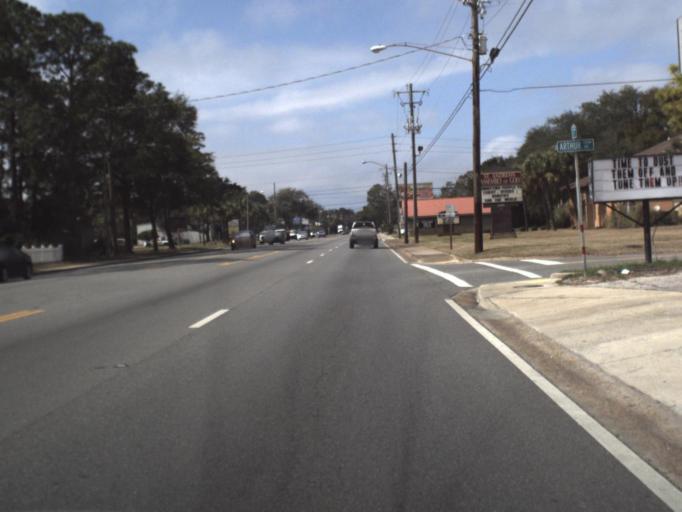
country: US
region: Florida
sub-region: Bay County
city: Pretty Bayou
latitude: 30.1755
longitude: -85.6949
